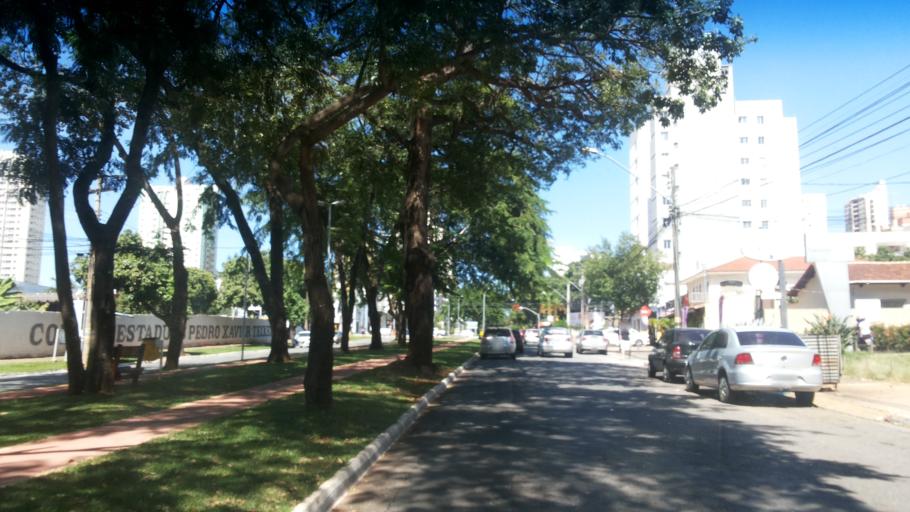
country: BR
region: Goias
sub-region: Goiania
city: Goiania
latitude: -16.7125
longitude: -49.2588
